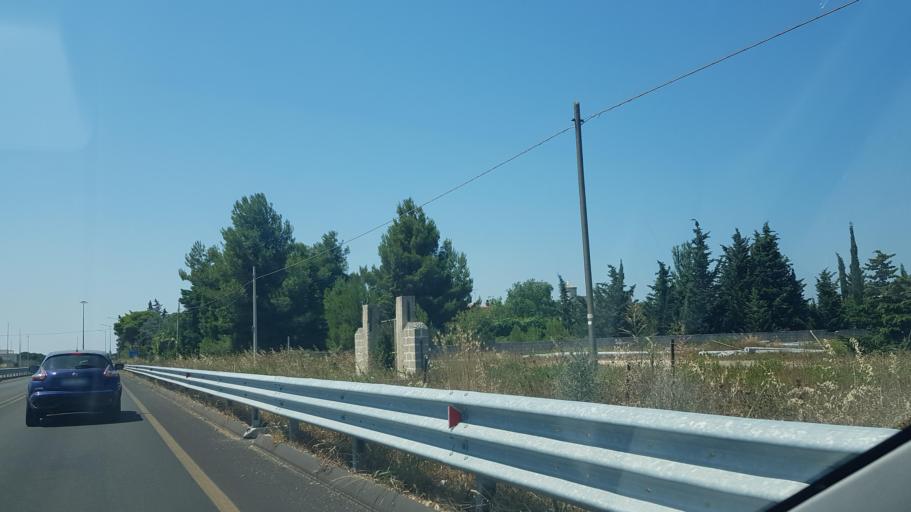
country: IT
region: Apulia
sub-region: Provincia di Lecce
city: Merine
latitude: 40.3337
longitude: 18.2402
